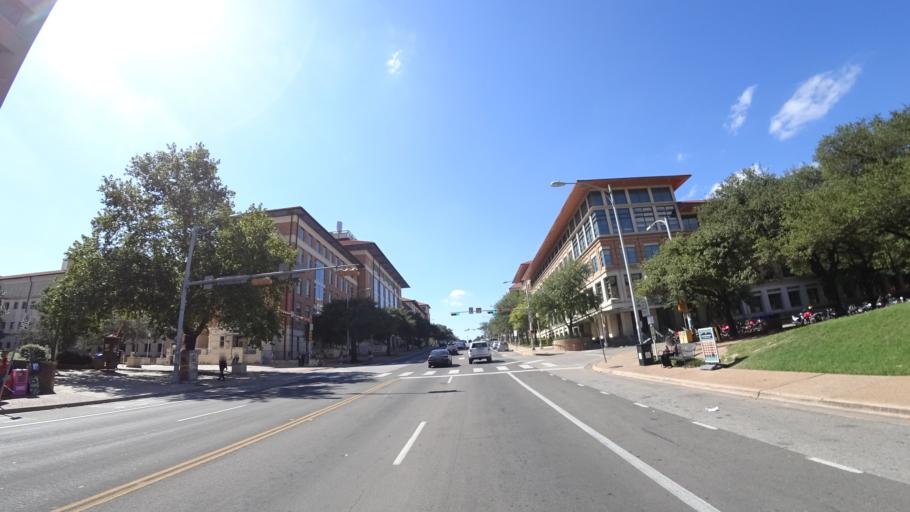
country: US
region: Texas
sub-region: Travis County
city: Austin
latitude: 30.2895
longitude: -97.7364
